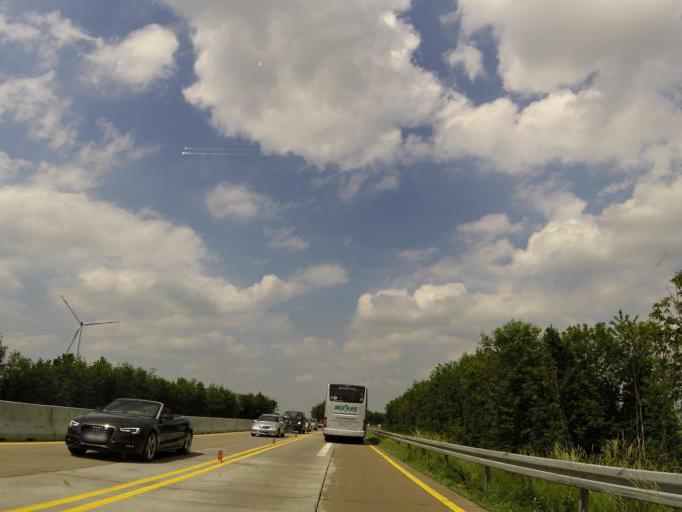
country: DE
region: Bavaria
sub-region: Regierungsbezirk Mittelfranken
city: Simmershofen
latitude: 49.5475
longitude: 10.1642
